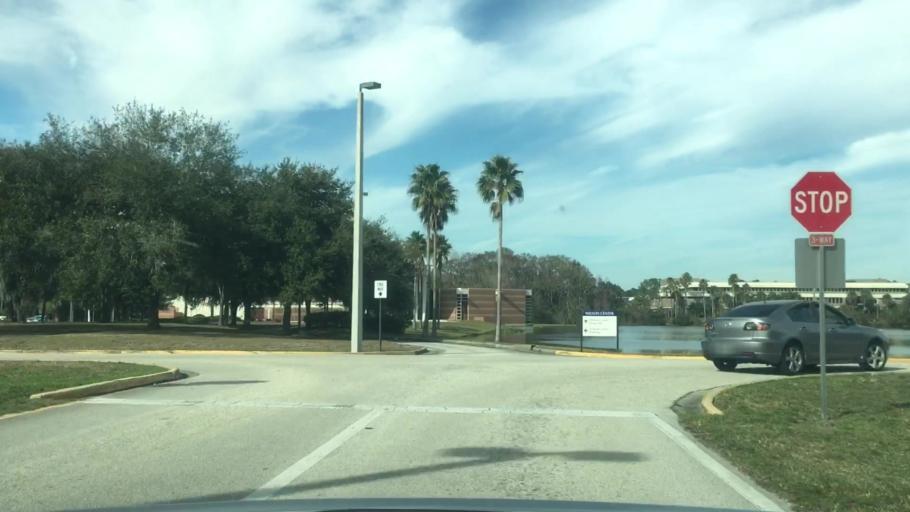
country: US
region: Florida
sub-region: Duval County
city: Neptune Beach
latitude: 30.2886
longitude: -81.5104
